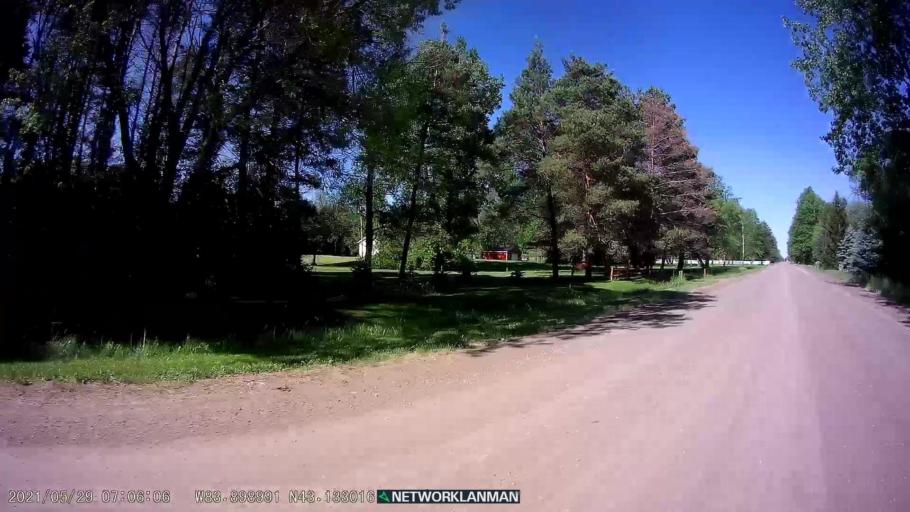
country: US
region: Michigan
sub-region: Genesee County
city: Montrose
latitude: 43.1330
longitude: -83.8994
